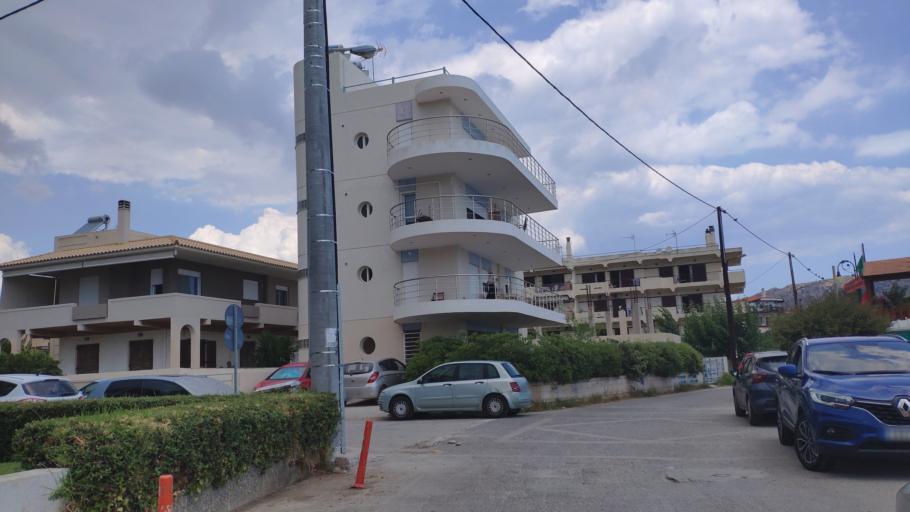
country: GR
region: Attica
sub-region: Nomarchia Anatolikis Attikis
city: Limin Mesoyaias
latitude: 37.8829
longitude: 24.0141
